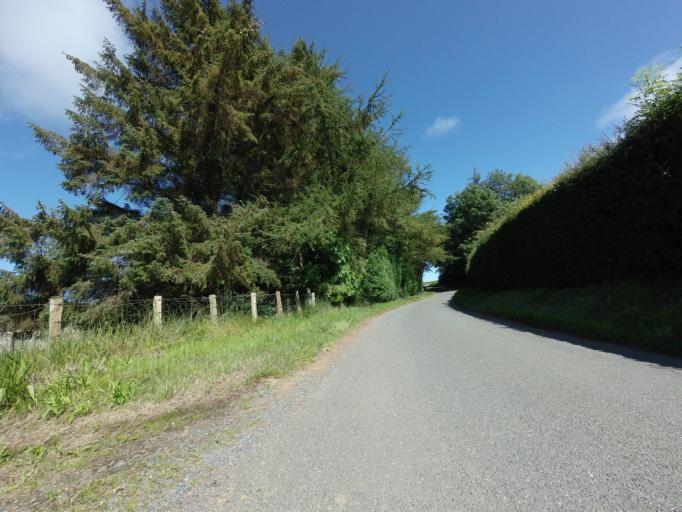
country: GB
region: Scotland
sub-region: Aberdeenshire
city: Banff
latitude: 57.6169
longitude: -2.5092
